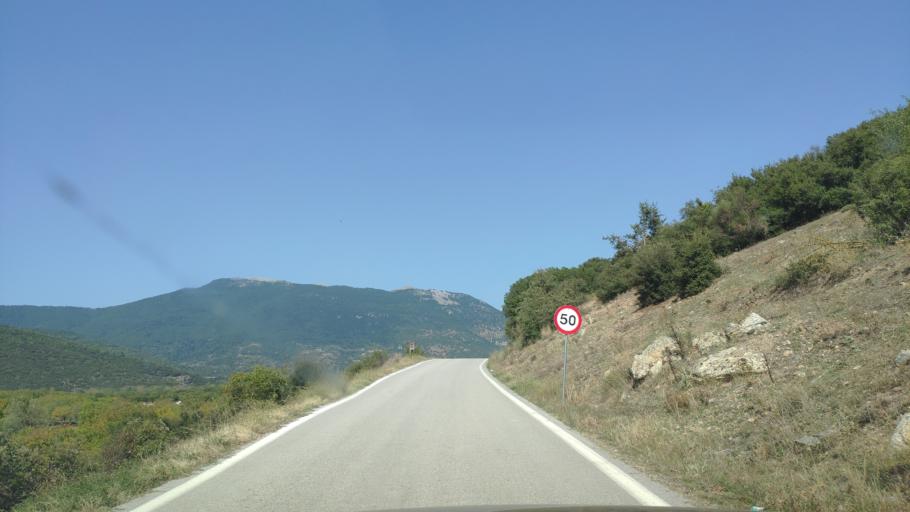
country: GR
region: West Greece
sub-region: Nomos Achaias
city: Aiyira
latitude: 37.9142
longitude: 22.3294
